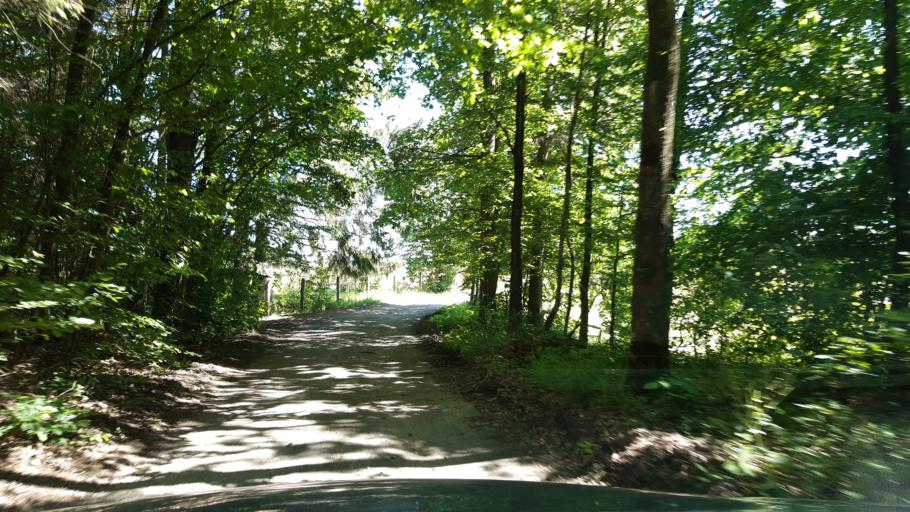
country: PL
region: Warmian-Masurian Voivodeship
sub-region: Powiat piski
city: Ruciane-Nida
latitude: 53.7061
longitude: 21.4751
